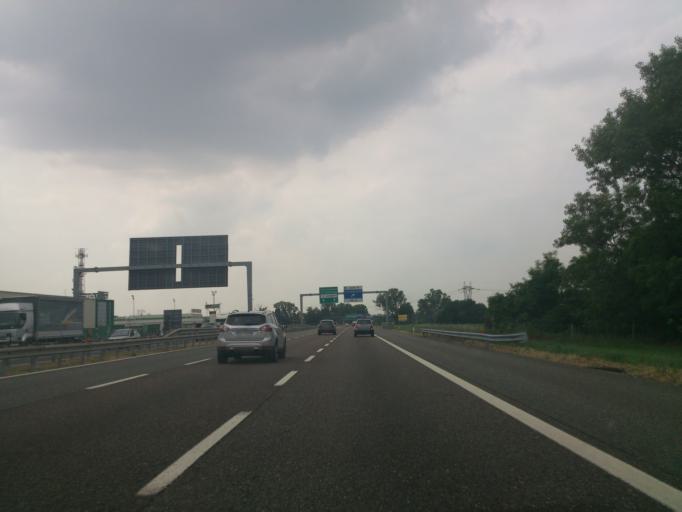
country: IT
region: Lombardy
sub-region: Citta metropolitana di Milano
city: Carugate
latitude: 45.5538
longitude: 9.3286
